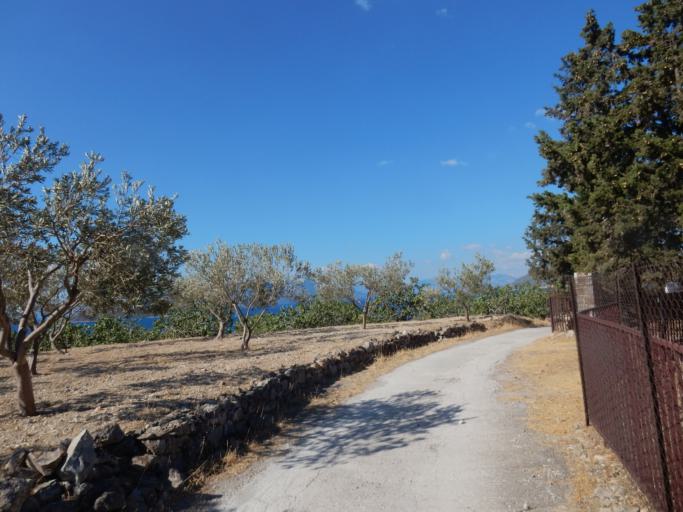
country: GR
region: Attica
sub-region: Nomos Piraios
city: Kypseli
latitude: 37.7319
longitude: 23.4519
